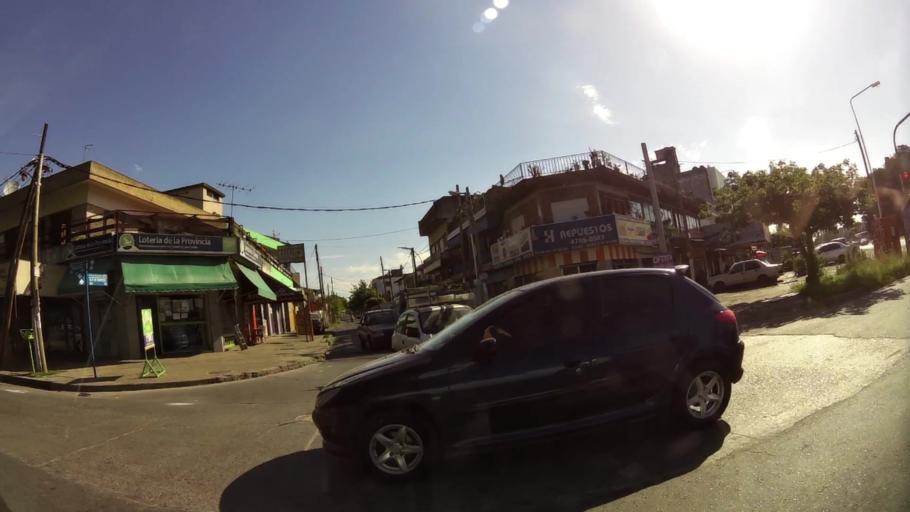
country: AR
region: Buenos Aires
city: Hurlingham
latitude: -34.5629
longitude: -58.5982
